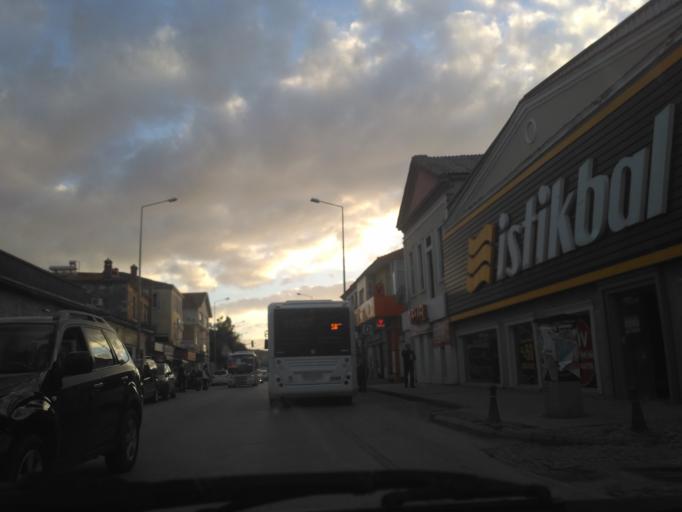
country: TR
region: Balikesir
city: Ayvalik
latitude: 39.3235
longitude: 26.6943
